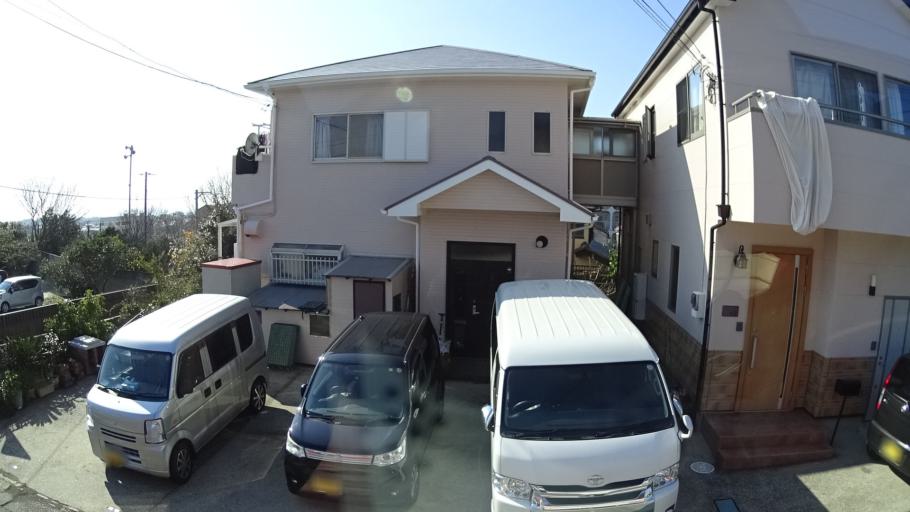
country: JP
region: Kanagawa
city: Miura
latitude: 35.1595
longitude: 139.6407
